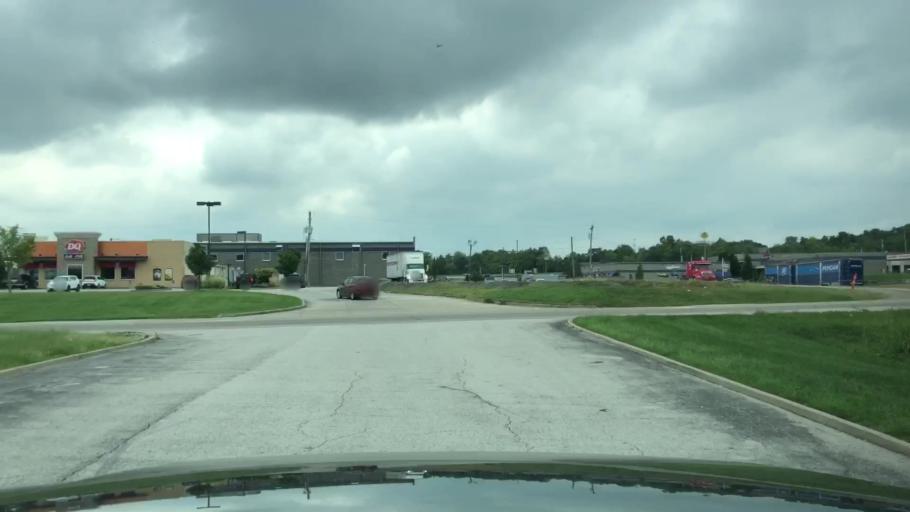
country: US
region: Missouri
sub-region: Saint Charles County
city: Saint Charles
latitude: 38.8077
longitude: -90.4757
